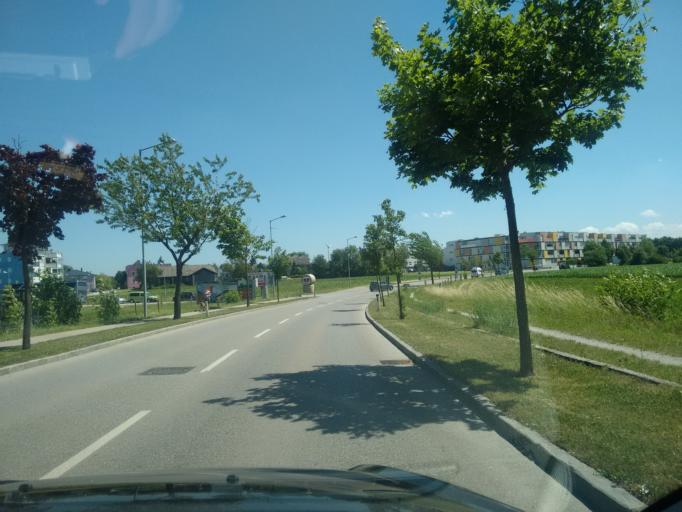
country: AT
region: Lower Austria
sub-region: Sankt Polten Stadt
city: Sankt Poelten
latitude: 48.2011
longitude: 15.6399
